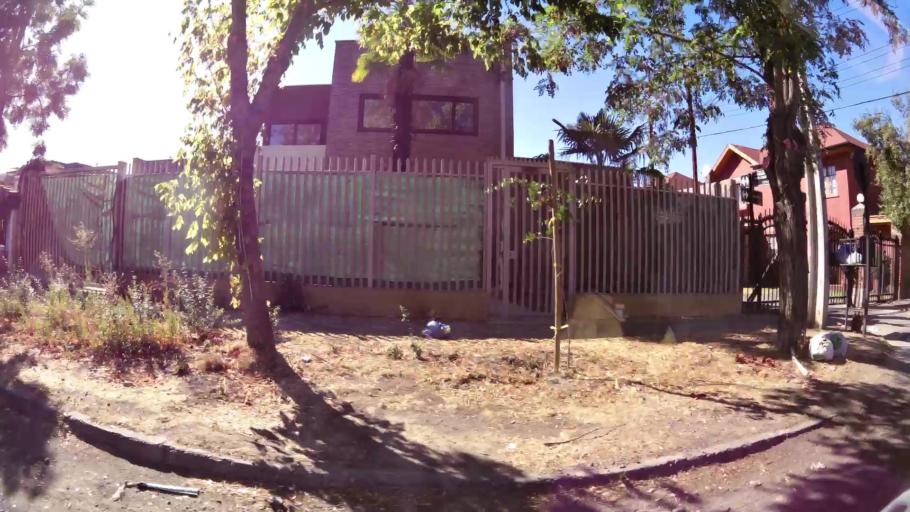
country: CL
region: O'Higgins
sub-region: Provincia de Cachapoal
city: Rancagua
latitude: -34.1799
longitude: -70.7144
